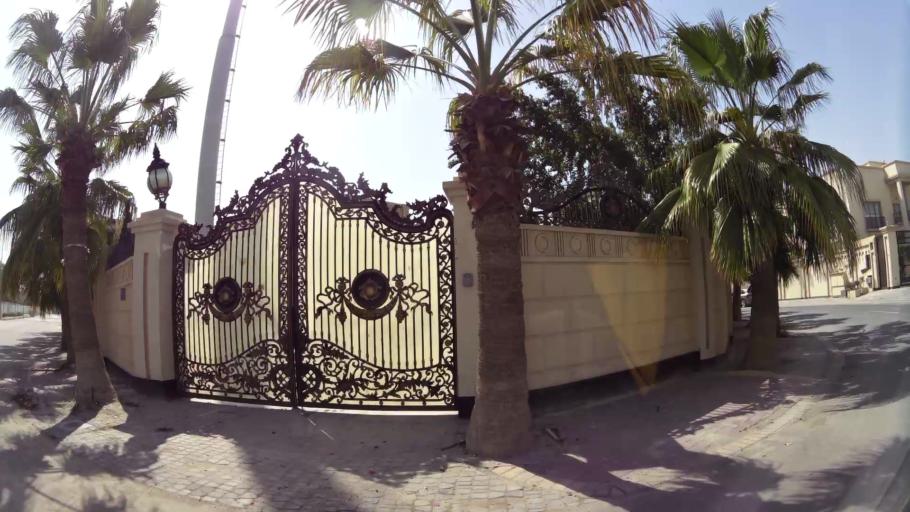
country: BH
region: Northern
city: Madinat `Isa
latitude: 26.1937
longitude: 50.4613
